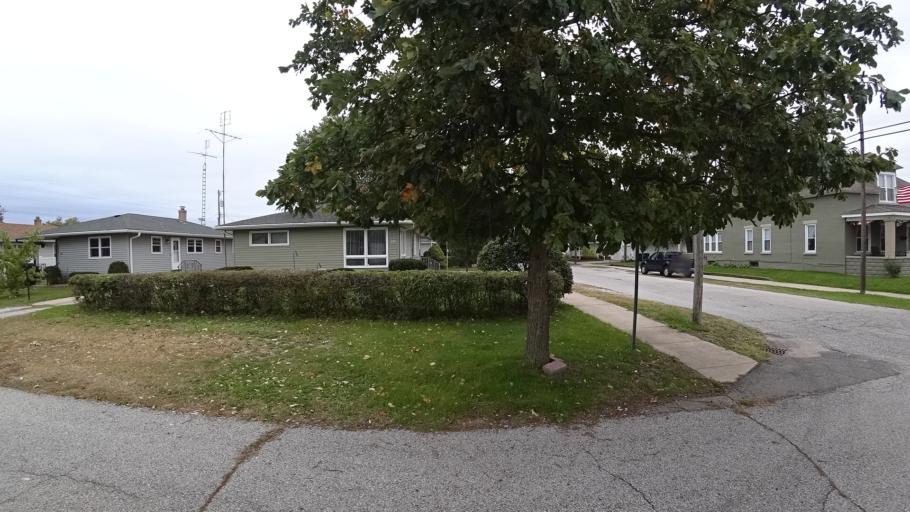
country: US
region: Indiana
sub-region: LaPorte County
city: Michigan City
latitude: 41.6998
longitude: -86.8976
